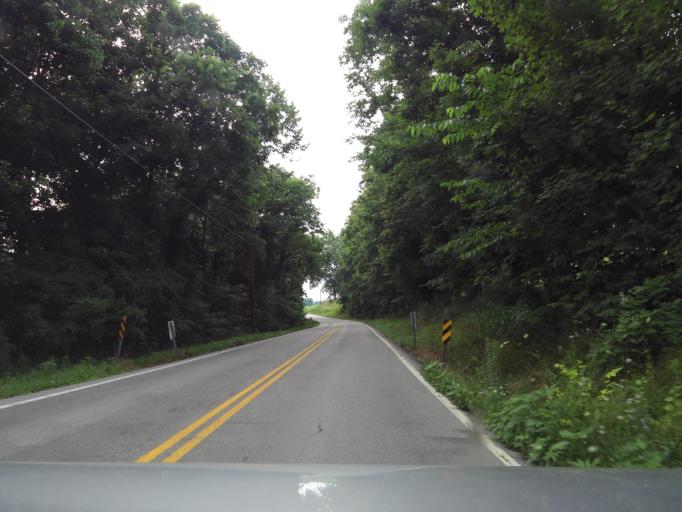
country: US
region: Kentucky
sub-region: Robertson County
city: Mount Olivet
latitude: 38.5118
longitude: -84.1535
